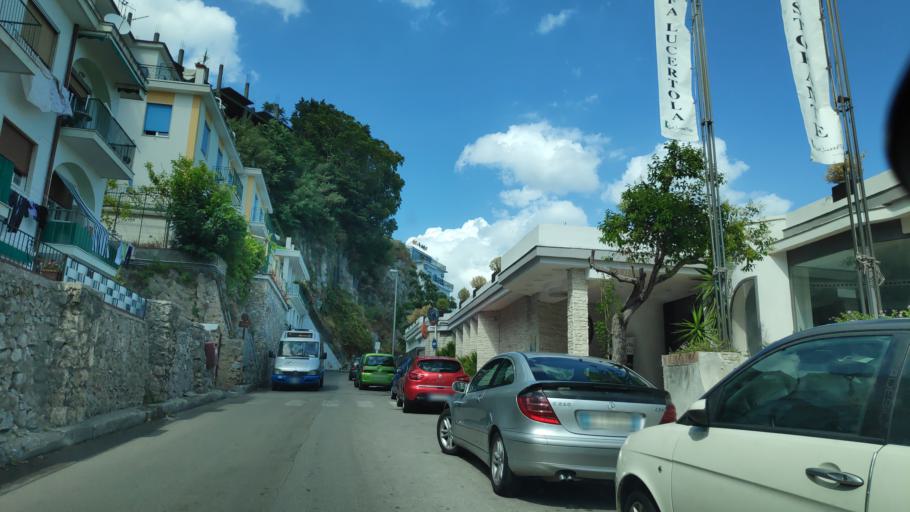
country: IT
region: Campania
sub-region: Provincia di Salerno
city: Vietri sul Mare
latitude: 40.6685
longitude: 14.7295
